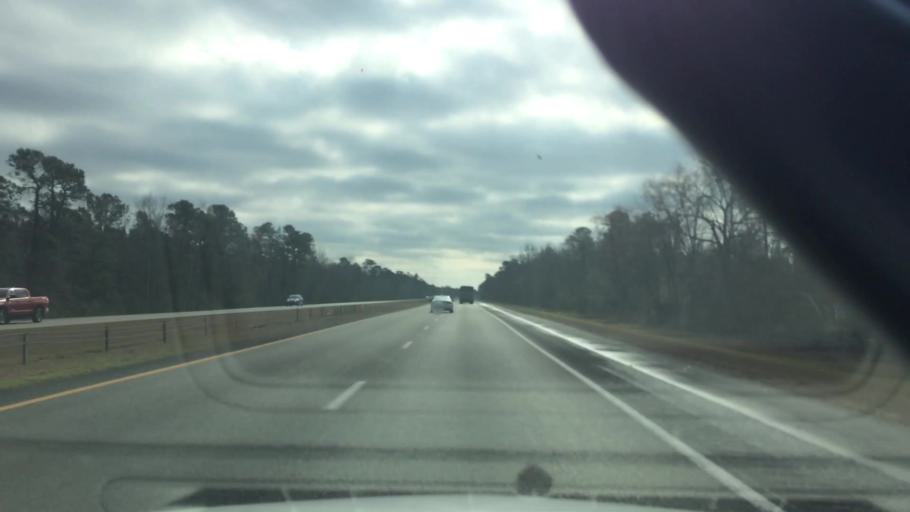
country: US
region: North Carolina
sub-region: Pender County
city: Rocky Point
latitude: 34.4045
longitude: -77.8720
